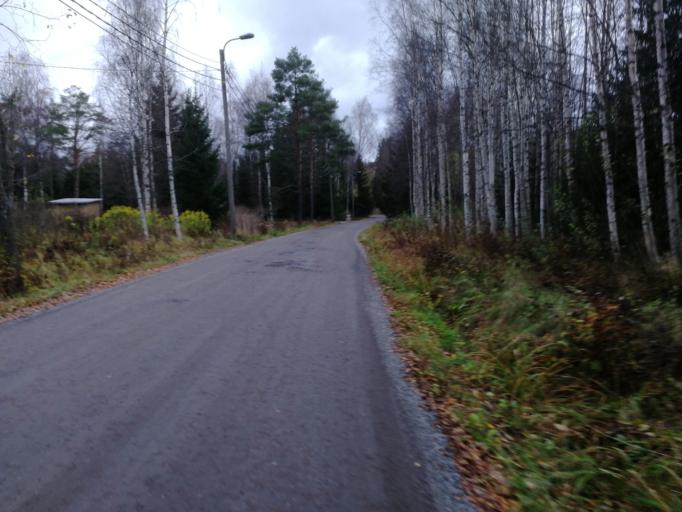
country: FI
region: Pirkanmaa
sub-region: Tampere
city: Tampere
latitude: 61.4542
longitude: 23.8896
